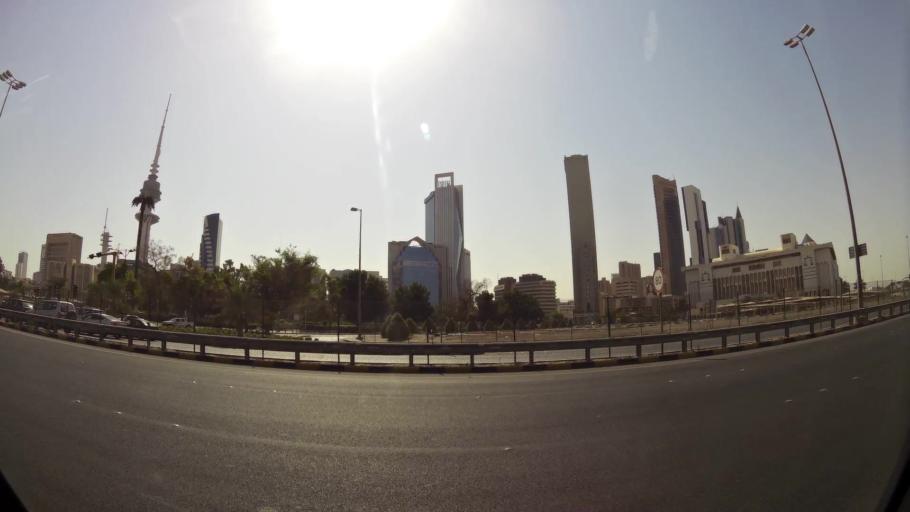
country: KW
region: Al Asimah
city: Kuwait City
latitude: 29.3721
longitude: 47.9690
